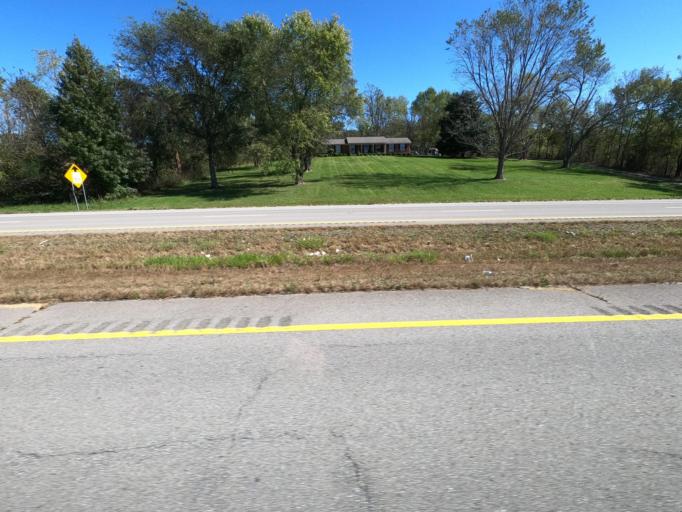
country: US
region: Tennessee
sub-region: Maury County
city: Mount Pleasant
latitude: 35.4177
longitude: -87.2821
